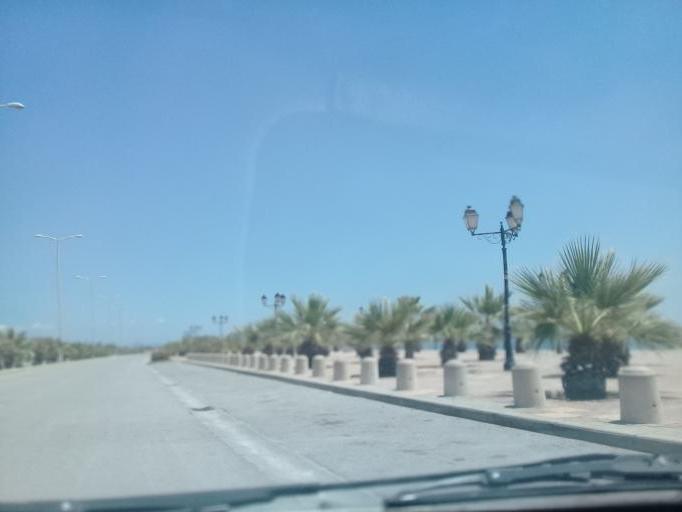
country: TN
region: Tunis
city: La Goulette
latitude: 36.8416
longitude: 10.2796
